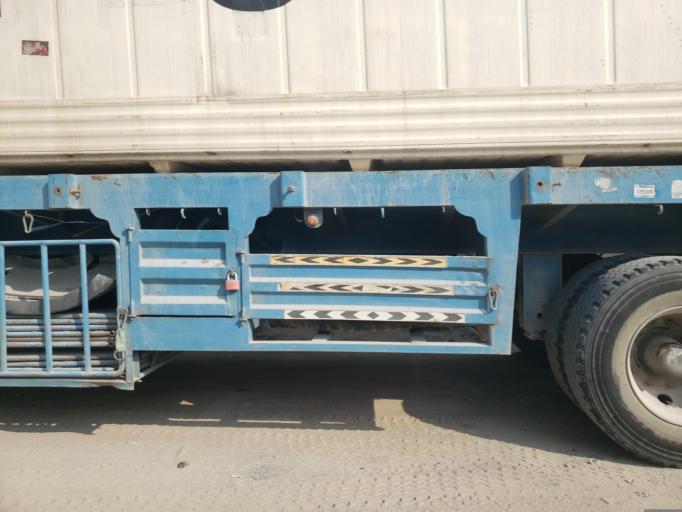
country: AE
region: Dubai
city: Dubai
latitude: 24.9857
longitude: 55.1093
